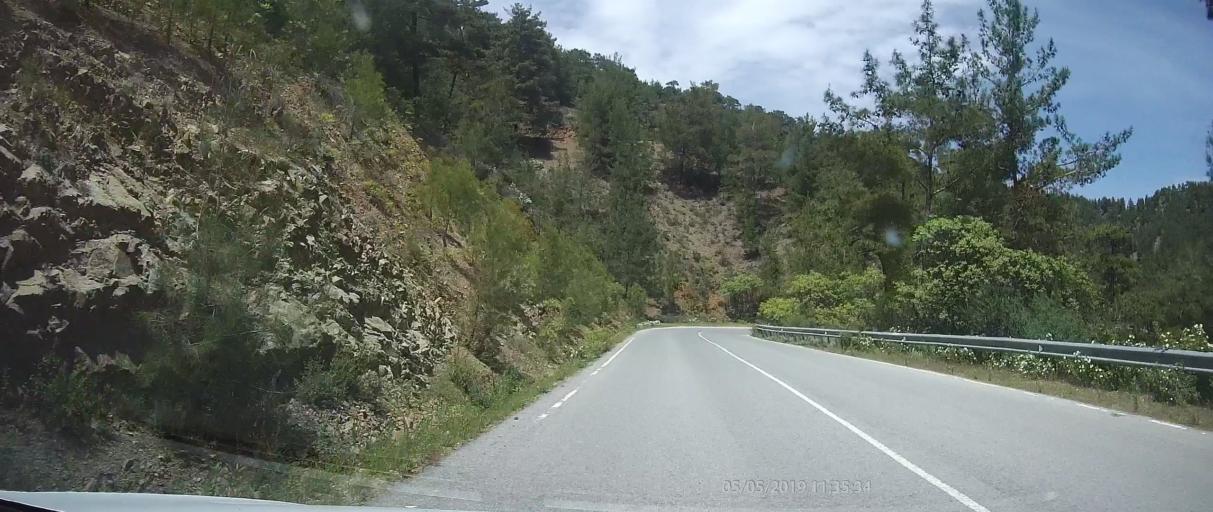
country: CY
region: Lefkosia
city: Kato Pyrgos
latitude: 34.9681
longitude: 32.6520
